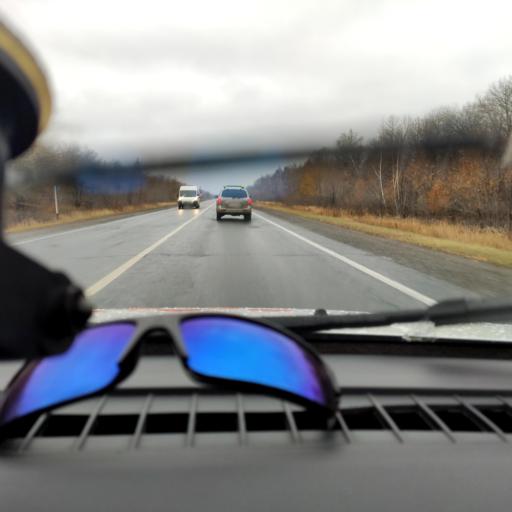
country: RU
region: Samara
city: Novokuybyshevsk
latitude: 52.9883
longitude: 49.8555
